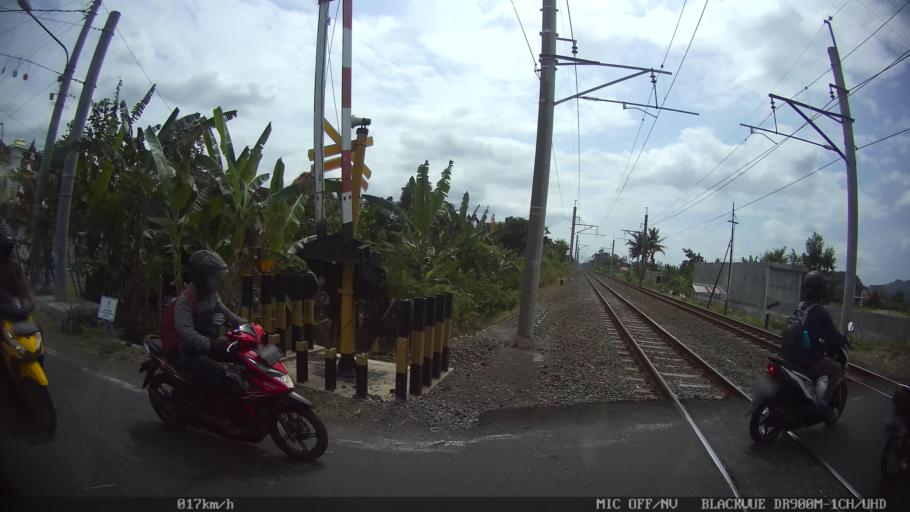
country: ID
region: Central Java
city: Candi Prambanan
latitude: -7.7721
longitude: 110.4693
